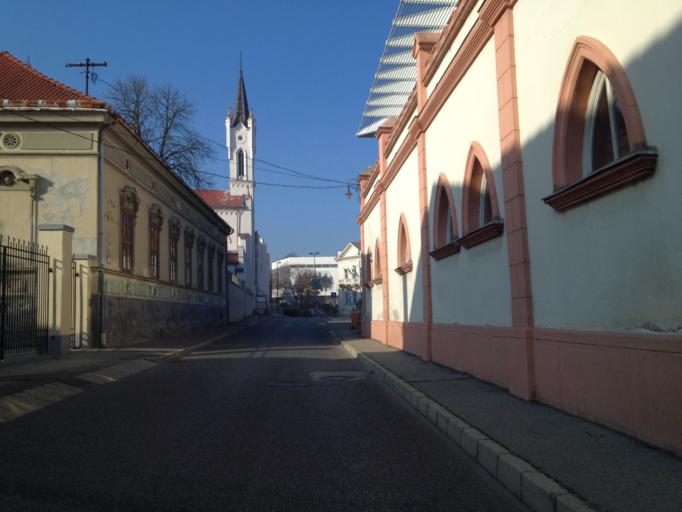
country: HU
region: Veszprem
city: Veszprem
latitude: 47.0906
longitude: 17.9061
